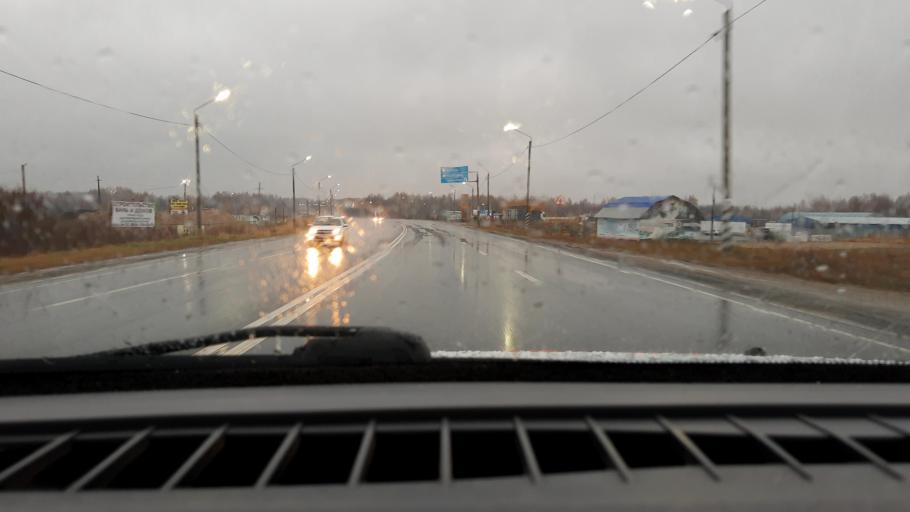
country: RU
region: Nizjnij Novgorod
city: Sitniki
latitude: 56.4991
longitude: 44.0253
